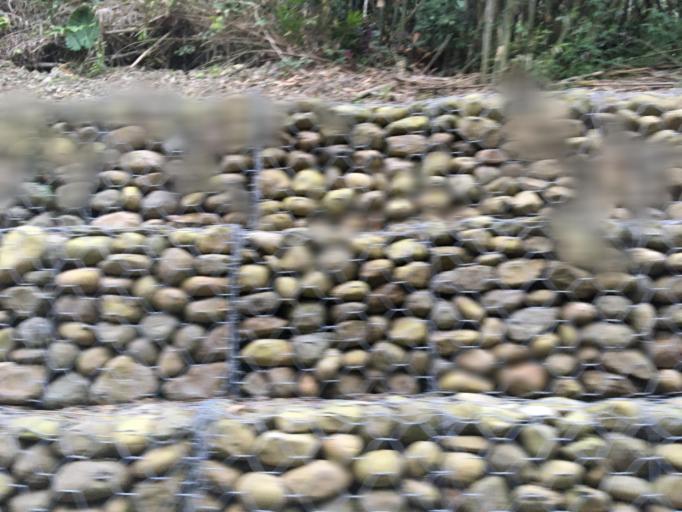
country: TW
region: Taiwan
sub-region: Yunlin
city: Douliu
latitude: 23.5477
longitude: 120.6111
